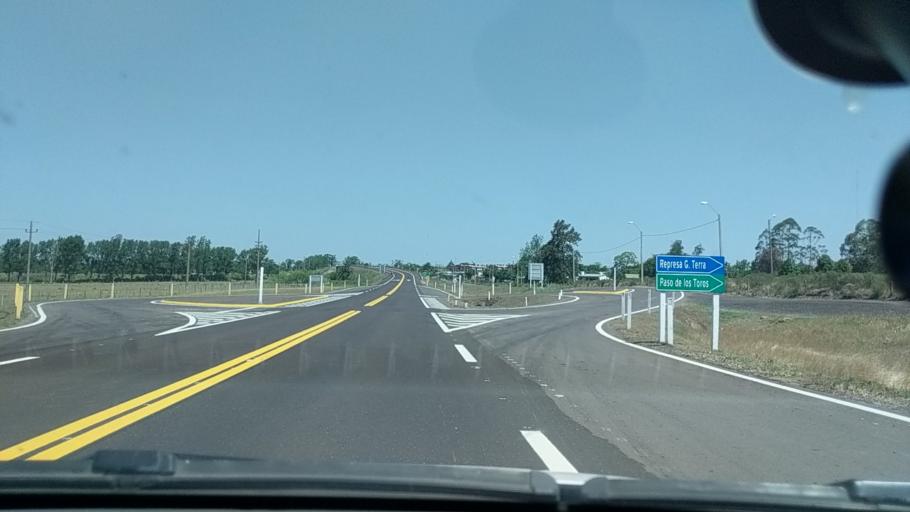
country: UY
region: Tacuarembo
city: Paso de los Toros
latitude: -32.8022
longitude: -56.5129
